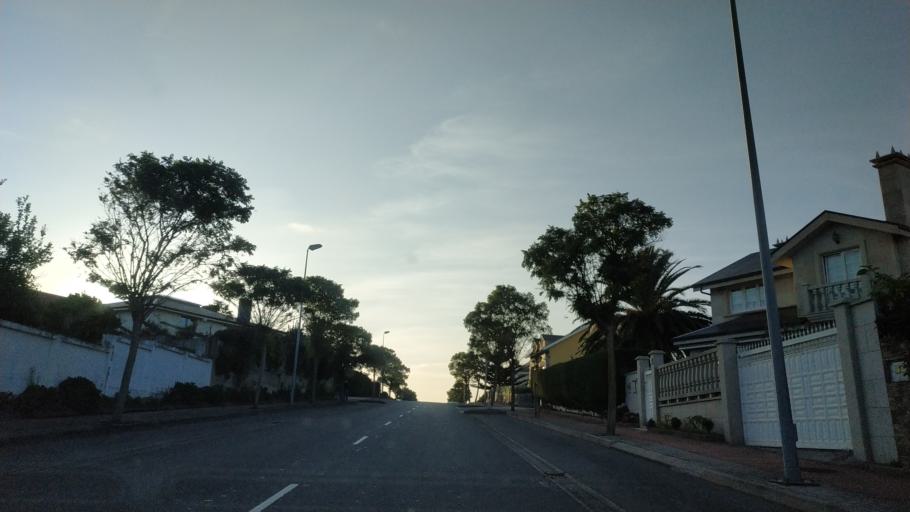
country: ES
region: Galicia
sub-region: Provincia da Coruna
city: Oleiros
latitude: 43.3706
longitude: -8.3405
